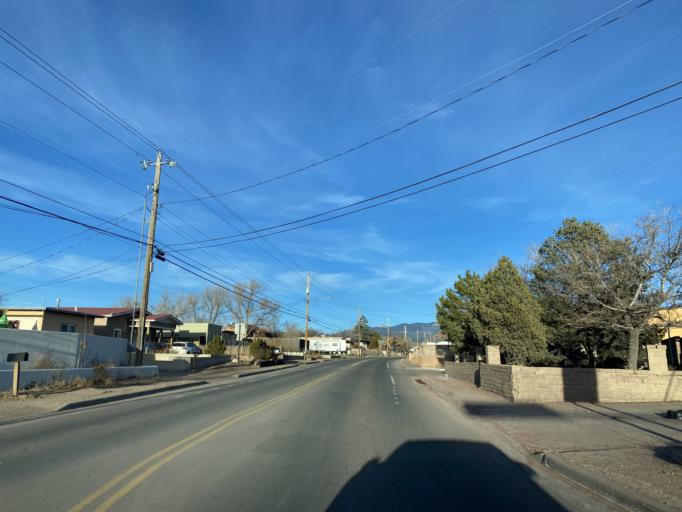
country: US
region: New Mexico
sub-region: Santa Fe County
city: Santa Fe
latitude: 35.6783
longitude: -105.9684
